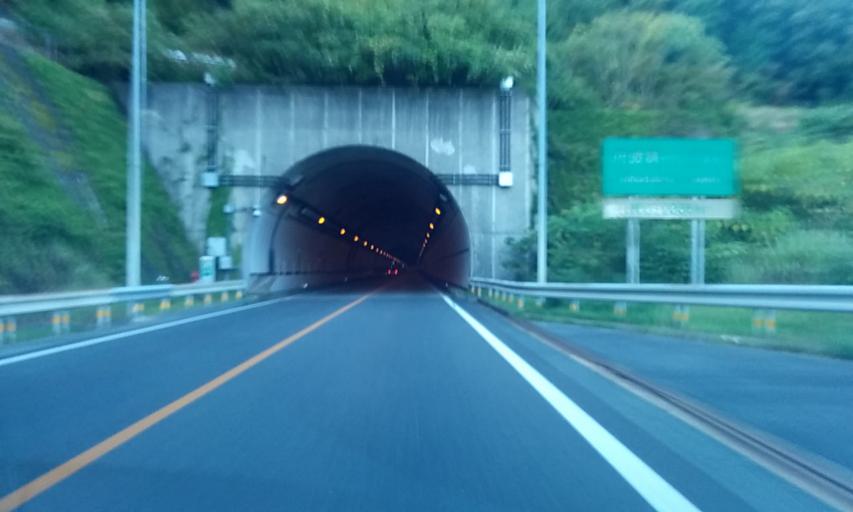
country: JP
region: Hyogo
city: Sasayama
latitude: 35.1159
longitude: 135.1653
